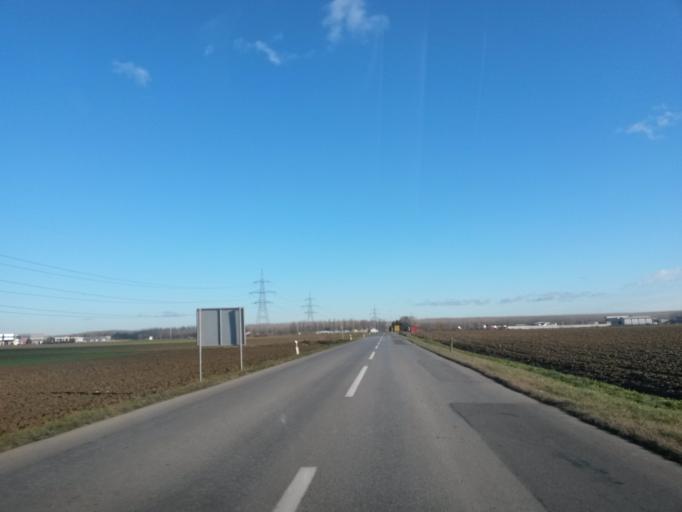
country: HR
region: Osjecko-Baranjska
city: Josipovac
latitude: 45.5898
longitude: 18.5639
